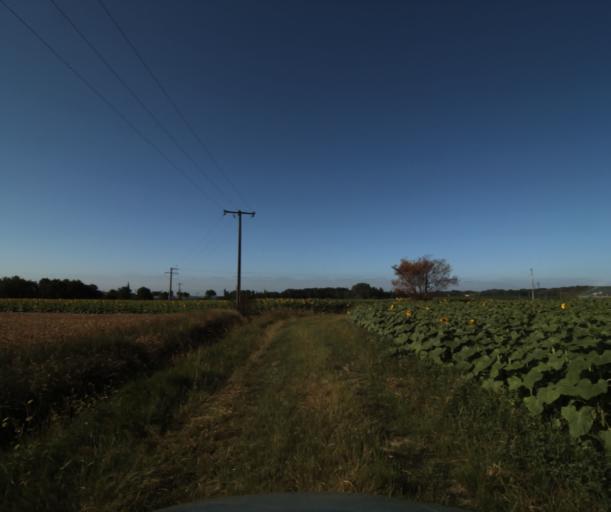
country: FR
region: Midi-Pyrenees
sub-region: Departement de la Haute-Garonne
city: Labarthe-sur-Leze
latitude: 43.4460
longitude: 1.3814
